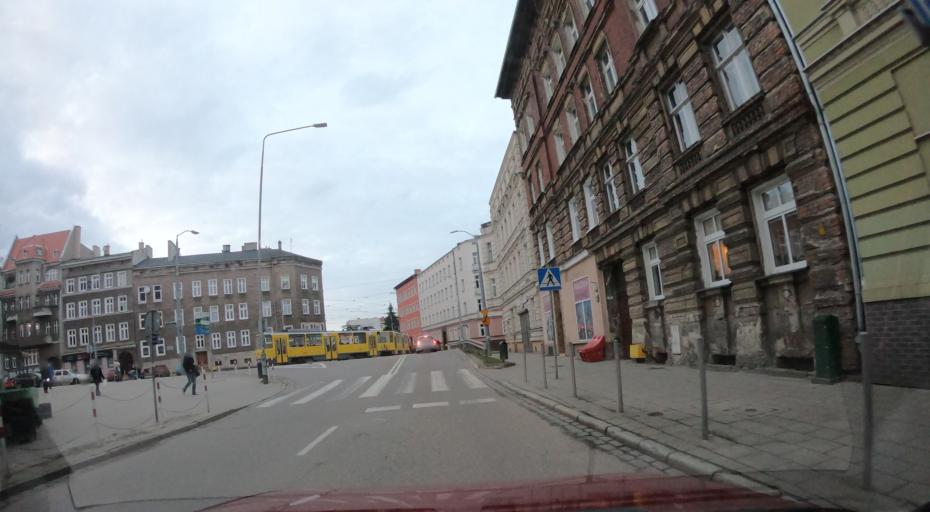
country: PL
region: West Pomeranian Voivodeship
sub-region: Szczecin
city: Szczecin
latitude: 53.4352
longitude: 14.5682
